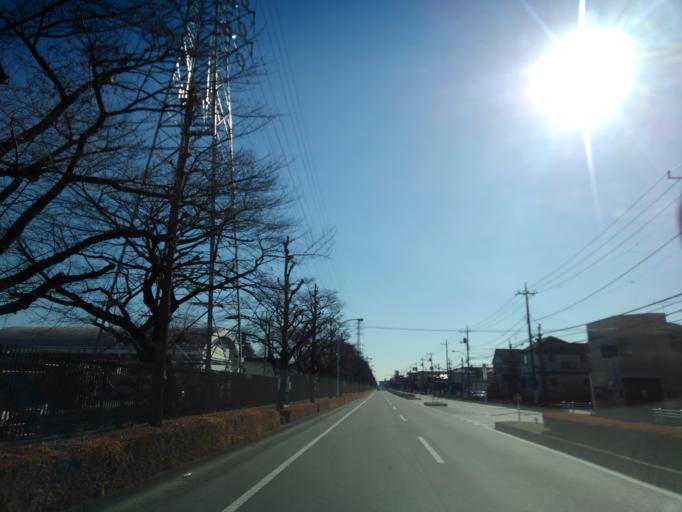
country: JP
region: Tokyo
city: Fussa
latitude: 35.7707
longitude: 139.3163
